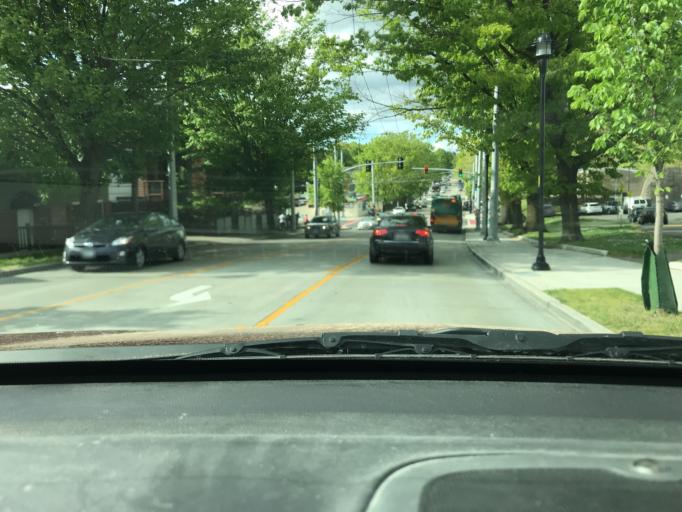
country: US
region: Washington
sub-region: King County
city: Seattle
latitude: 47.6054
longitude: -122.3027
